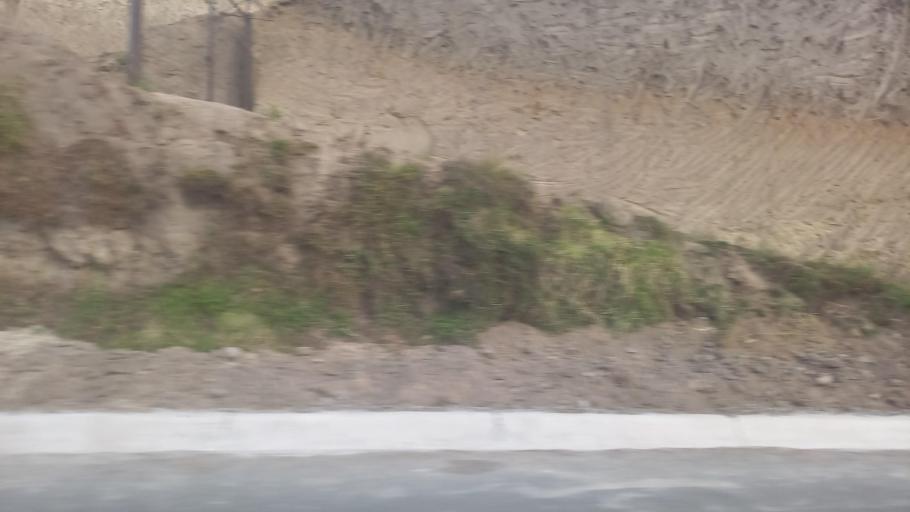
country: EC
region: Pichincha
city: Cayambe
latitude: 0.1234
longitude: -78.0753
